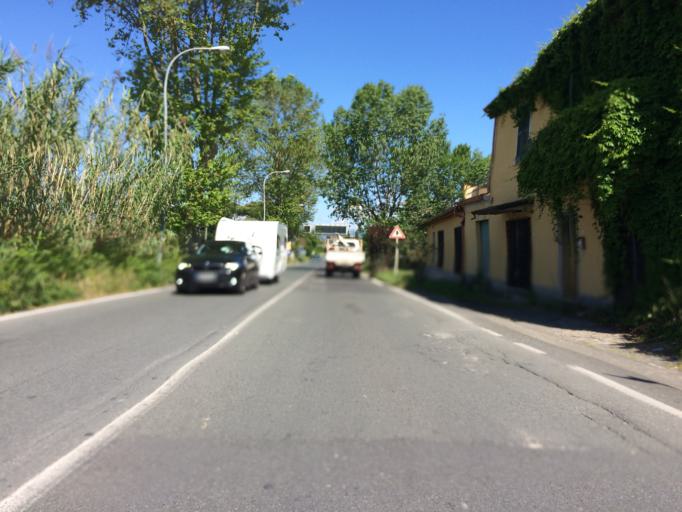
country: IT
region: Tuscany
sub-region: Provincia di Massa-Carrara
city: Borghetto-Melara
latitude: 44.0972
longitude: 9.9864
